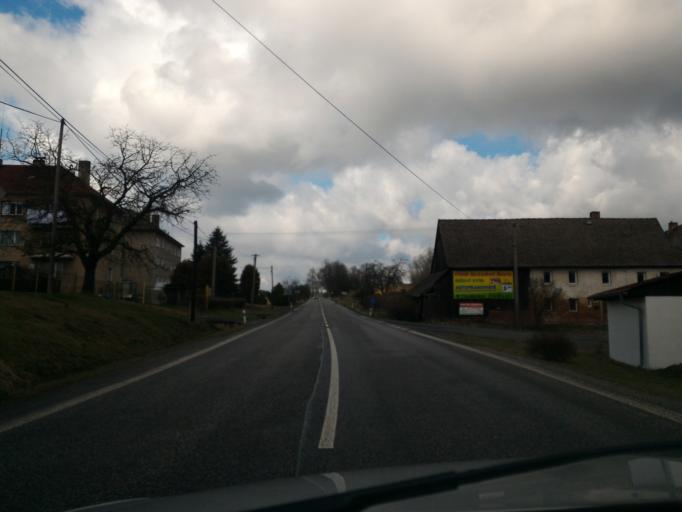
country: PL
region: Silesian Voivodeship
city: Zawidow
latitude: 50.9807
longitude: 15.0773
